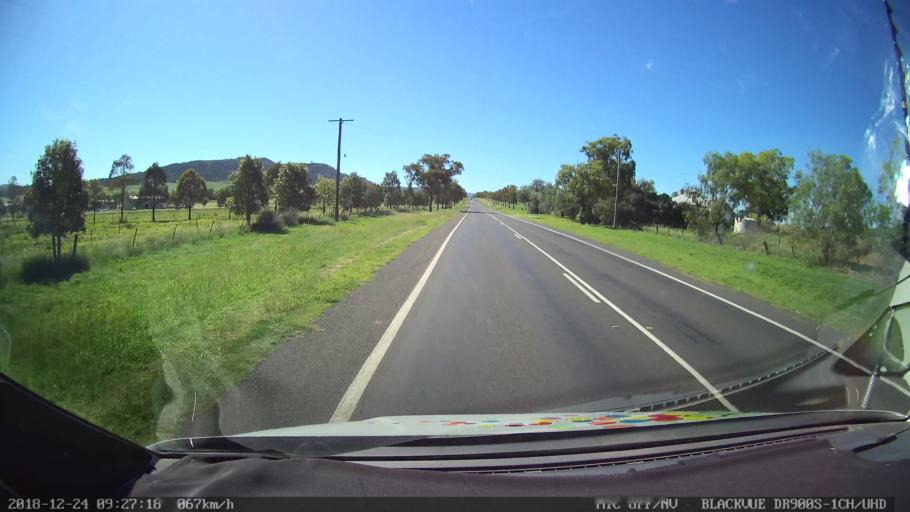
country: AU
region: New South Wales
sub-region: Liverpool Plains
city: Quirindi
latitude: -31.5268
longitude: 150.6802
